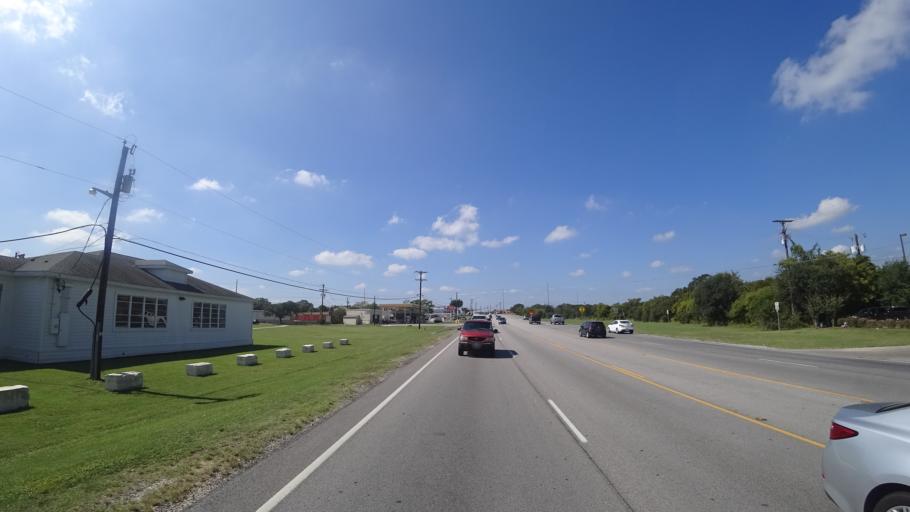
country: US
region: Texas
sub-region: Williamson County
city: Round Rock
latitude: 30.5119
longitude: -97.6974
